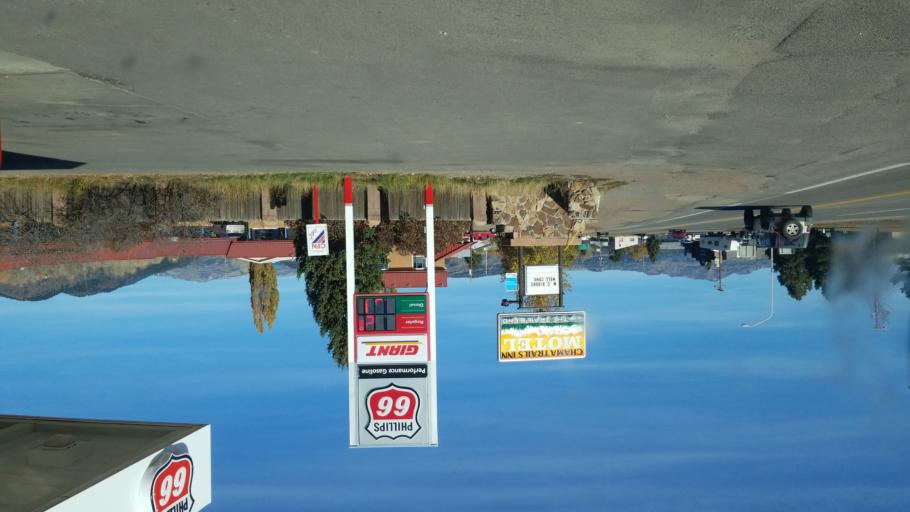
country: US
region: New Mexico
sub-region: Rio Arriba County
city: Chama
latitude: 36.8829
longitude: -106.5844
